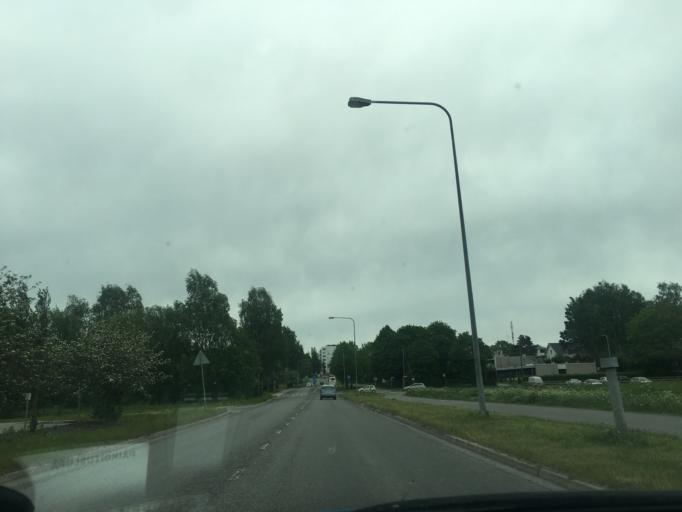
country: FI
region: Varsinais-Suomi
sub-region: Turku
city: Turku
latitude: 60.4617
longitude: 22.3051
